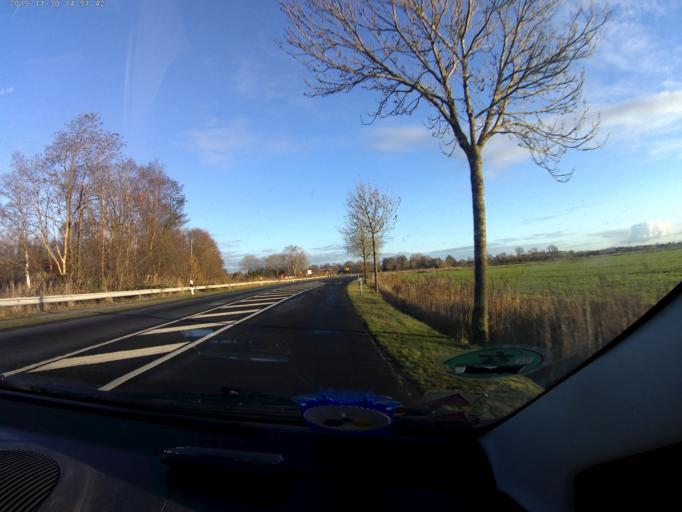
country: DE
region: Lower Saxony
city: Jemgum
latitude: 53.2619
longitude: 7.4248
